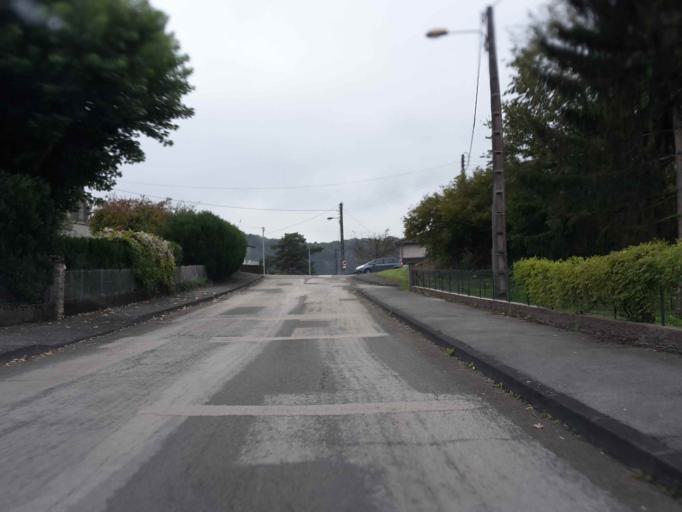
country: FR
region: Franche-Comte
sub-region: Departement du Doubs
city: Baume-les-Dames
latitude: 47.3475
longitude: 6.3688
